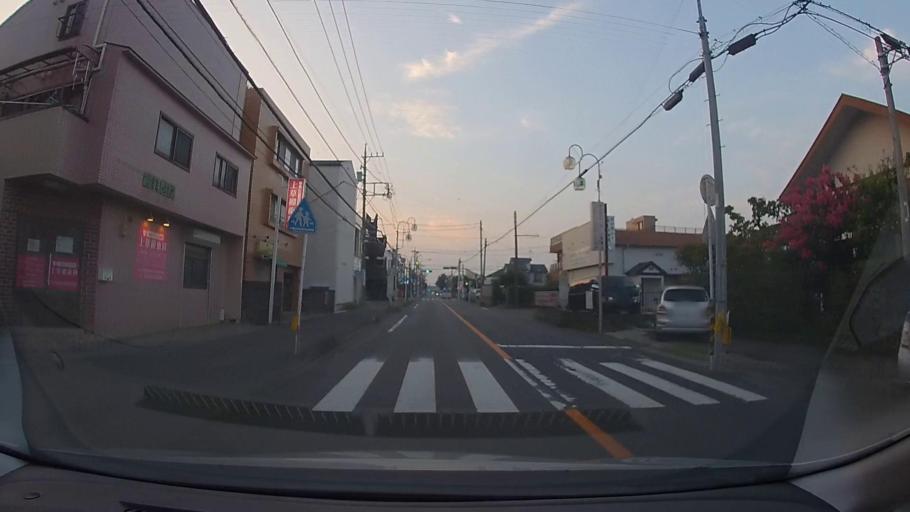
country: JP
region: Kanagawa
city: Minami-rinkan
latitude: 35.4753
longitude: 139.4550
